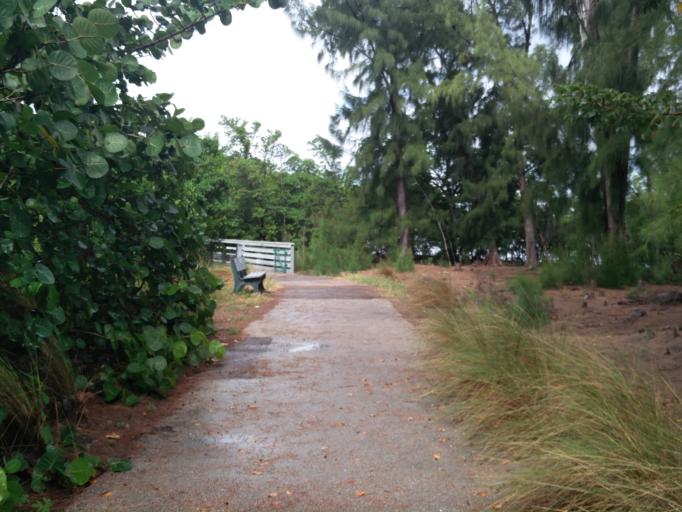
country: US
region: Florida
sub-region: Broward County
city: Dania Beach
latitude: 26.0388
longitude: -80.1179
